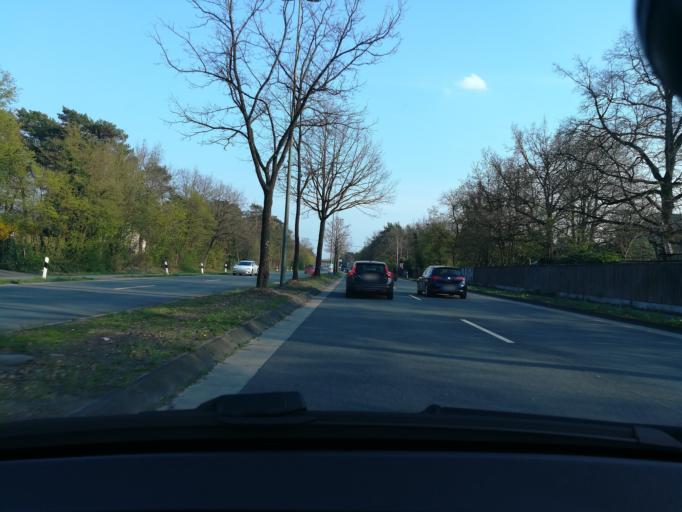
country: DE
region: North Rhine-Westphalia
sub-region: Regierungsbezirk Detmold
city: Bielefeld
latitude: 51.9623
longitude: 8.5613
